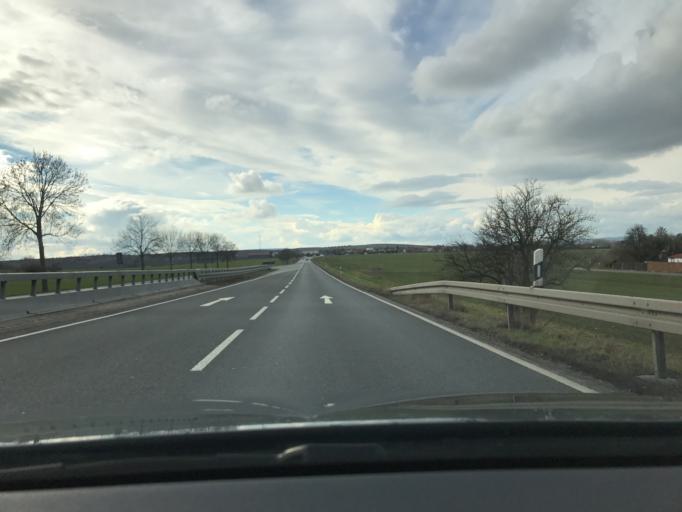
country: DE
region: Saxony-Anhalt
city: Roblingen am See
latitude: 51.4862
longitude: 11.6893
